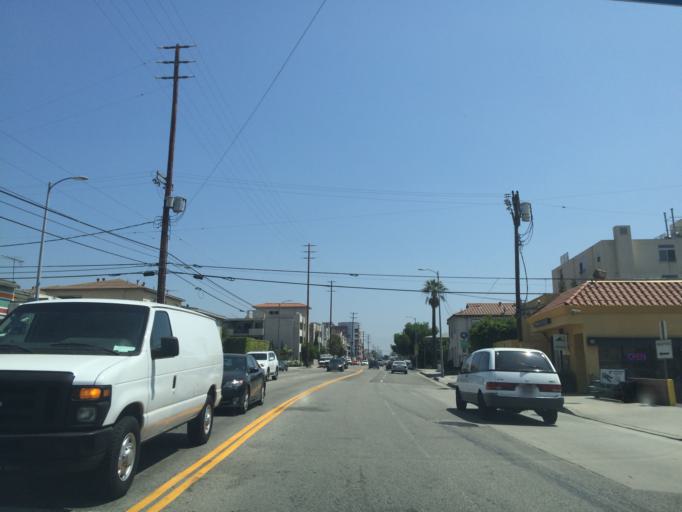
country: US
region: California
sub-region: Los Angeles County
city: Culver City
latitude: 34.0247
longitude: -118.4116
